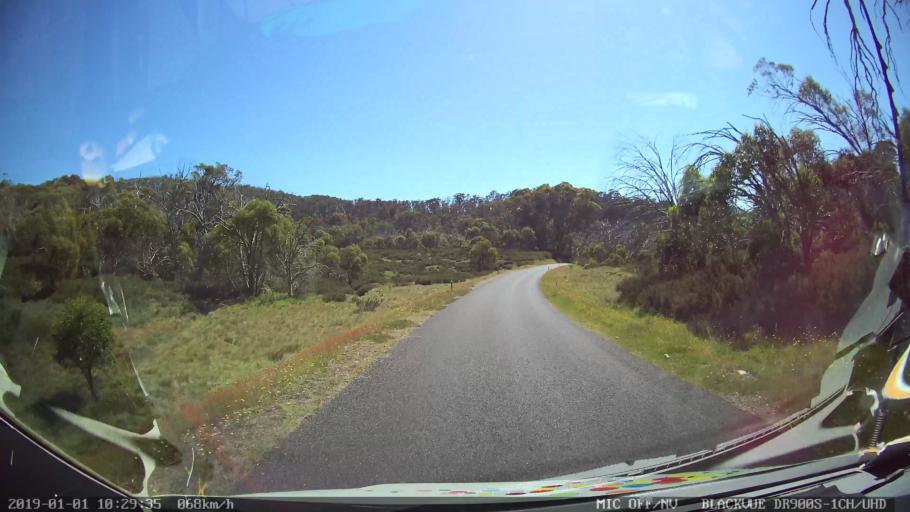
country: AU
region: New South Wales
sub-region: Snowy River
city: Jindabyne
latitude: -36.0532
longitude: 148.2486
